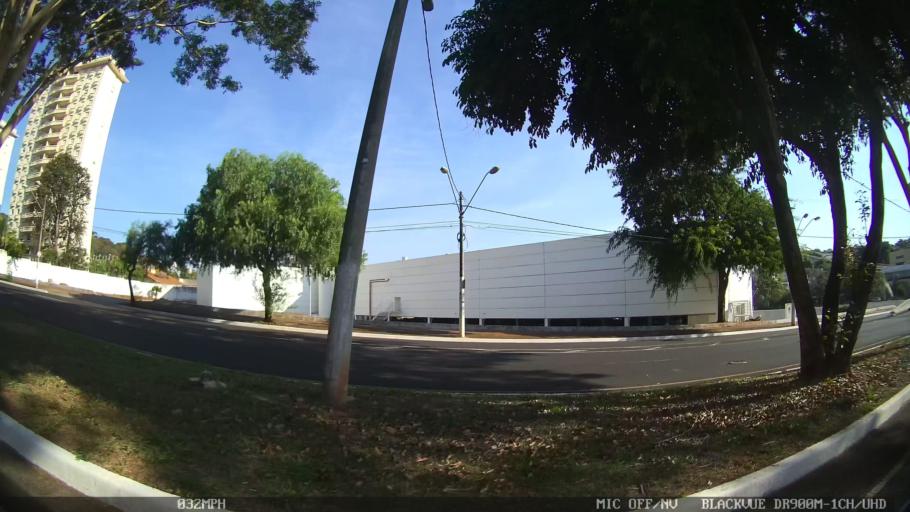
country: BR
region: Sao Paulo
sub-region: Ribeirao Preto
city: Ribeirao Preto
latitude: -21.1955
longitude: -47.7964
